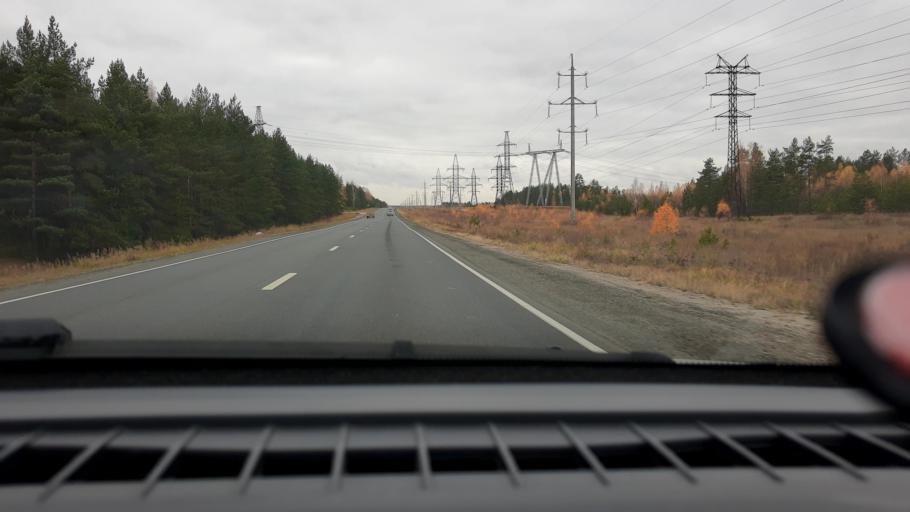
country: RU
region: Nizjnij Novgorod
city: Lukino
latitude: 56.3902
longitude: 43.6412
